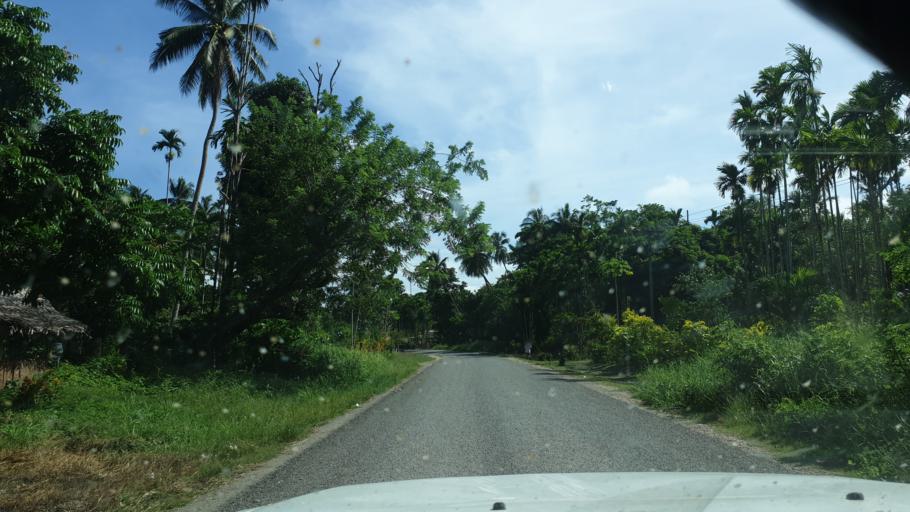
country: PG
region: Madang
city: Madang
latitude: -4.8221
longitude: 145.7729
